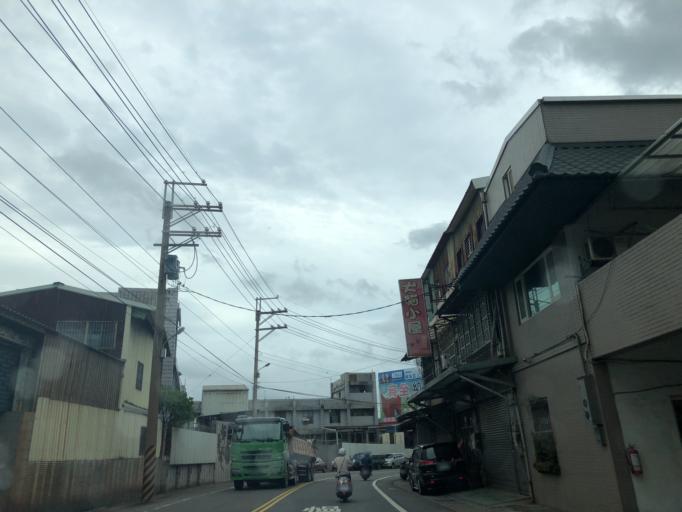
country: TW
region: Taiwan
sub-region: Taoyuan
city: Taoyuan
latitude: 24.9469
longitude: 121.3402
